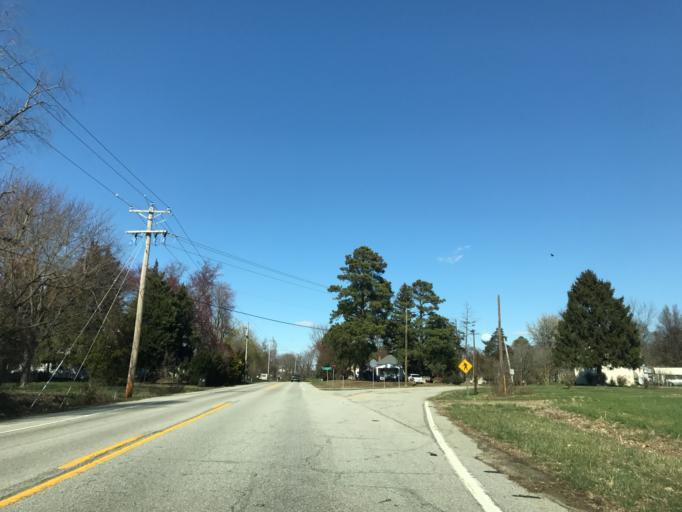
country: US
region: Maryland
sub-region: Kent County
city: Rock Hall
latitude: 39.2186
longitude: -76.1736
